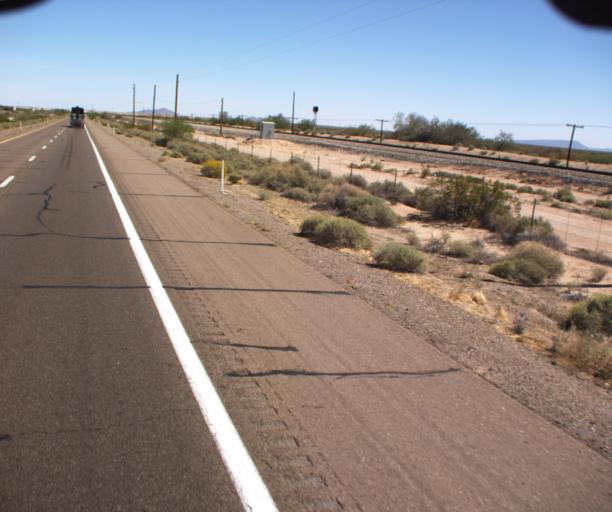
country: US
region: Arizona
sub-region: Yuma County
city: Wellton
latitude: 32.7477
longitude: -113.6689
